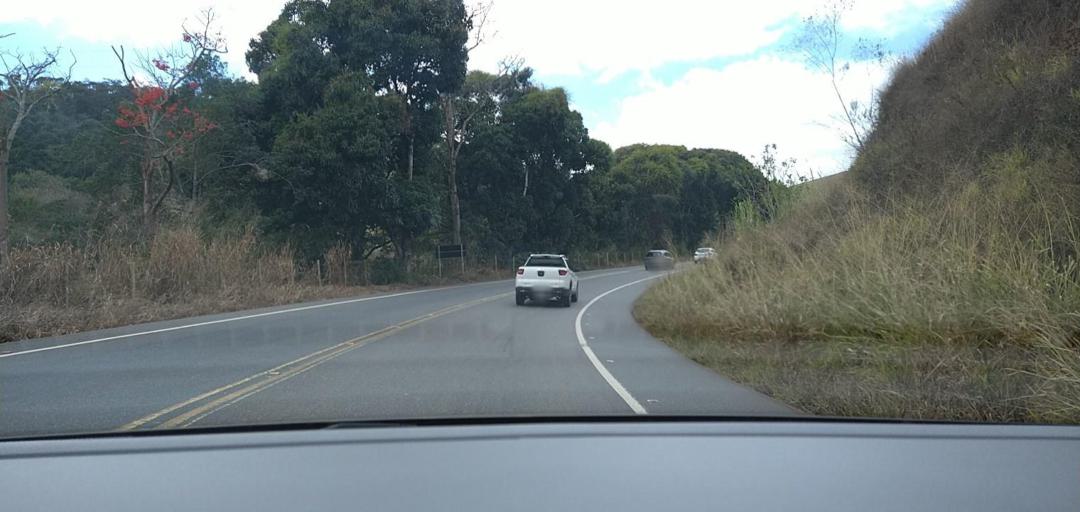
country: BR
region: Minas Gerais
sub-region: Ponte Nova
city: Ponte Nova
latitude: -20.5116
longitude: -42.8943
